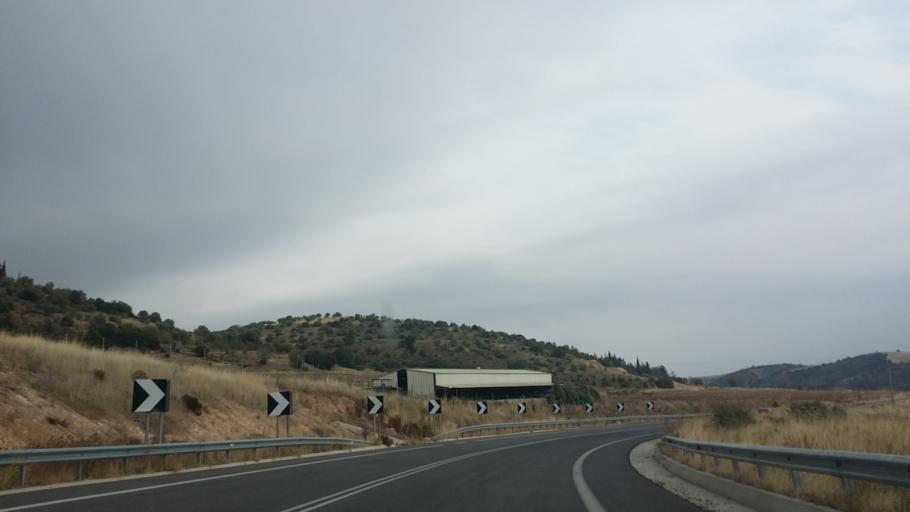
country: GR
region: Central Greece
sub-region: Nomos Voiotias
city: Vagia
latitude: 38.2990
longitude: 23.1918
